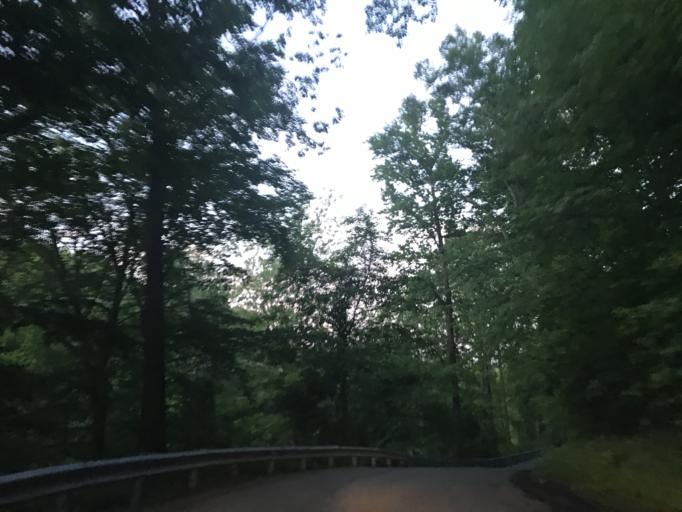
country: US
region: Maryland
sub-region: Harford County
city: Joppatowne
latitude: 39.4661
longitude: -76.3330
